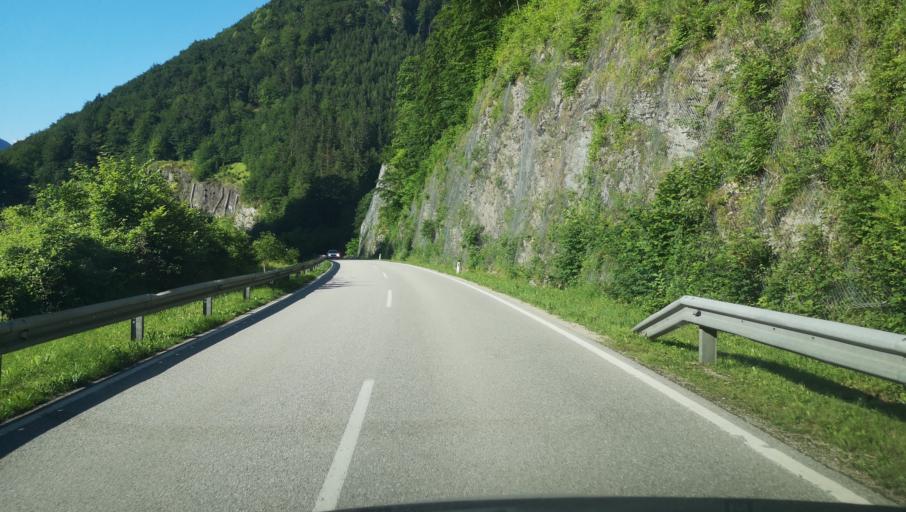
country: AT
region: Lower Austria
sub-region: Politischer Bezirk Amstetten
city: Ybbsitz
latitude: 47.9192
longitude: 14.8334
